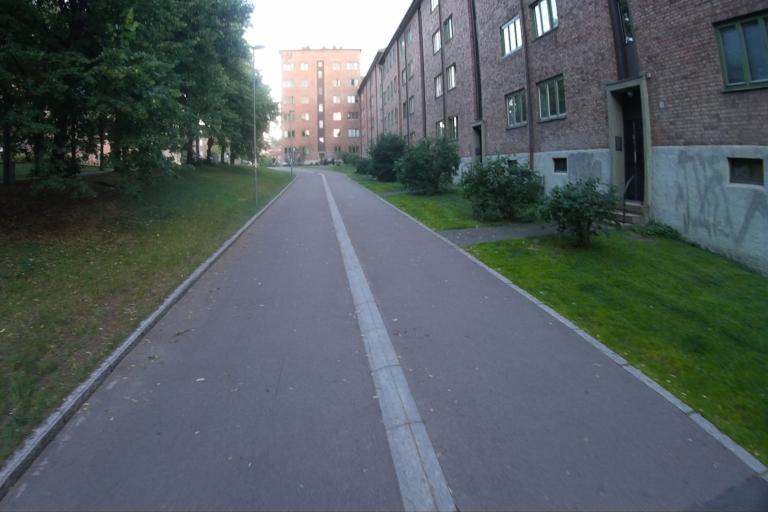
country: NO
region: Oslo
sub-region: Oslo
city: Oslo
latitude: 59.9278
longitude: 10.7722
